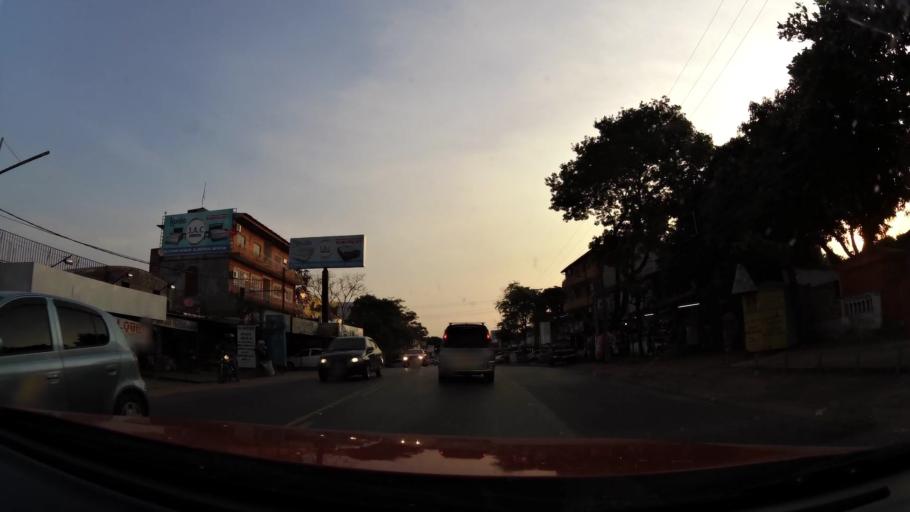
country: PY
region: Central
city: Villa Elisa
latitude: -25.3564
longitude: -57.5949
